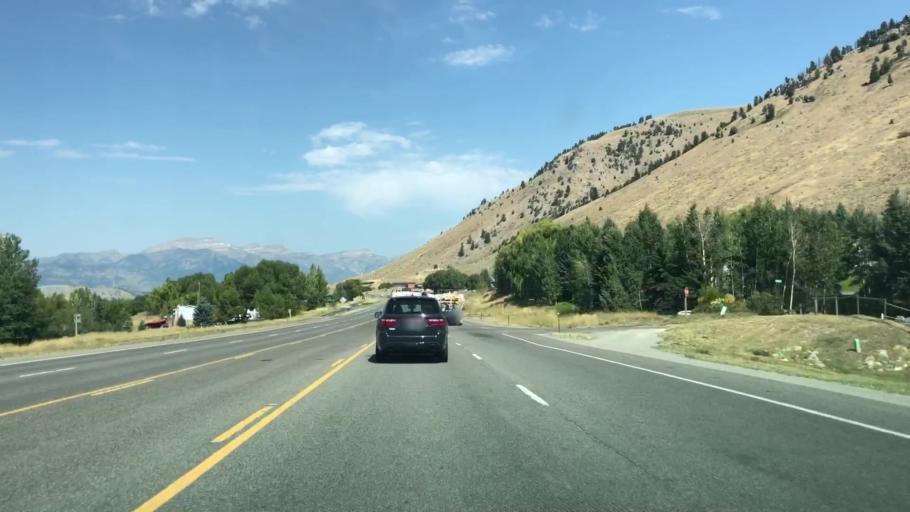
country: US
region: Wyoming
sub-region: Teton County
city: South Park
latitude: 43.4247
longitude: -110.7775
